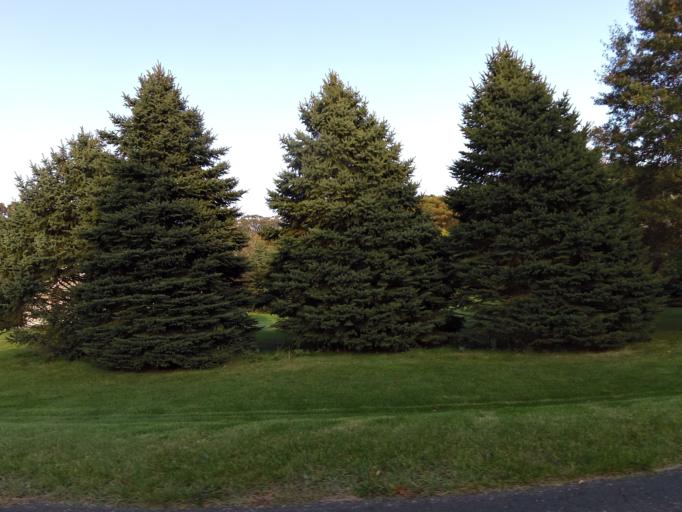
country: US
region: Minnesota
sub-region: Washington County
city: Bayport
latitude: 44.9822
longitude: -92.8057
